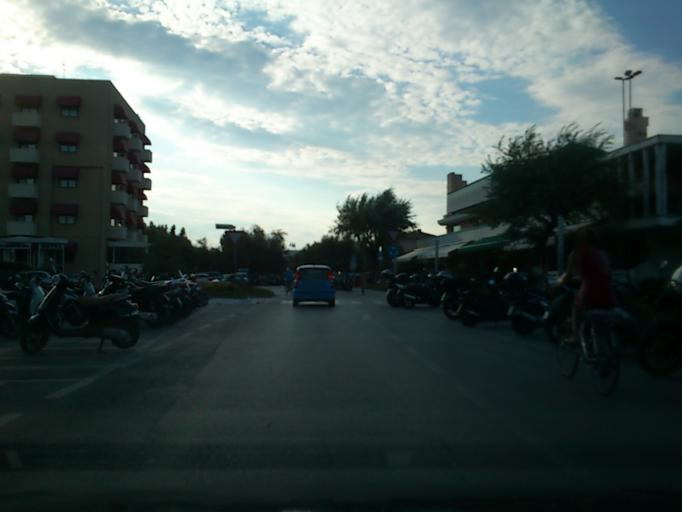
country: IT
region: The Marches
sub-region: Provincia di Pesaro e Urbino
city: Fano
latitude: 43.8508
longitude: 13.0115
